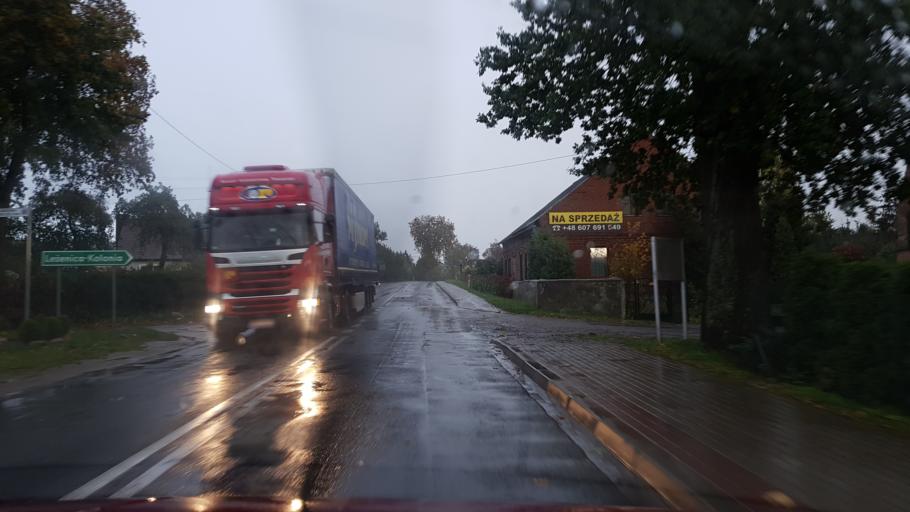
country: PL
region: Greater Poland Voivodeship
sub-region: Powiat pilski
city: Szydlowo
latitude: 53.1684
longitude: 16.5938
